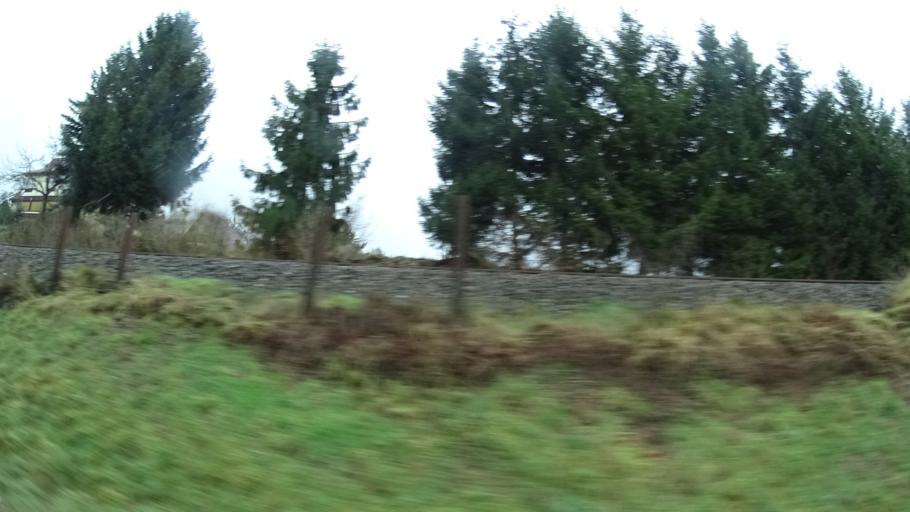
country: DE
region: Thuringia
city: Breitenbach
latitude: 50.7085
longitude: 10.4796
